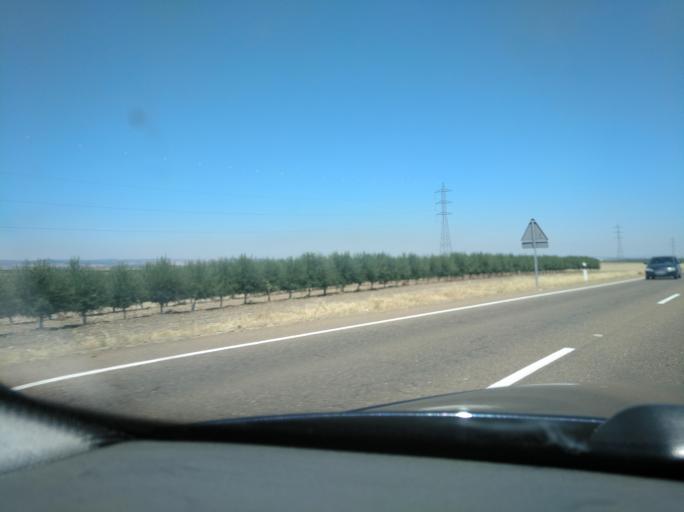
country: ES
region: Extremadura
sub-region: Provincia de Badajoz
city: Olivenza
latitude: 38.7637
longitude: -7.0652
